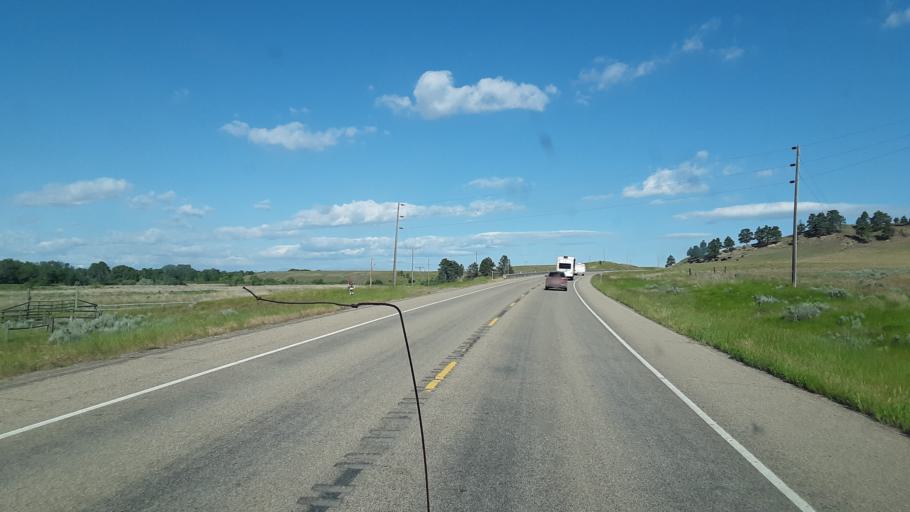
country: US
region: Montana
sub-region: Golden Valley County
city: Ryegate
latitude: 46.3196
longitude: -109.4317
